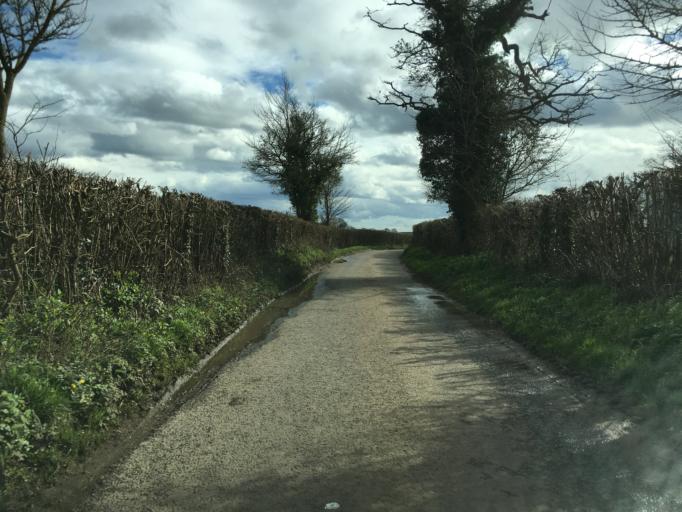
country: GB
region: England
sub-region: Gloucestershire
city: Newent
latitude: 51.8581
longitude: -2.3815
